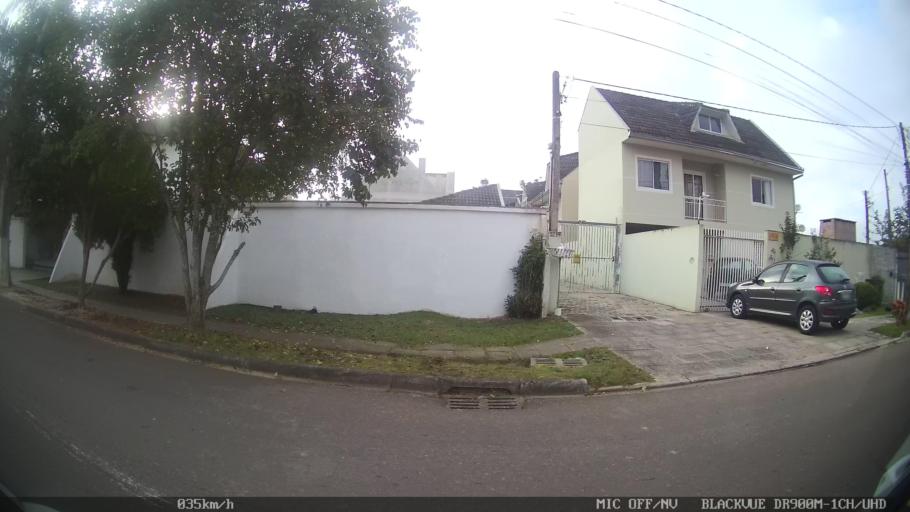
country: BR
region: Parana
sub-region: Almirante Tamandare
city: Almirante Tamandare
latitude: -25.3882
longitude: -49.3372
